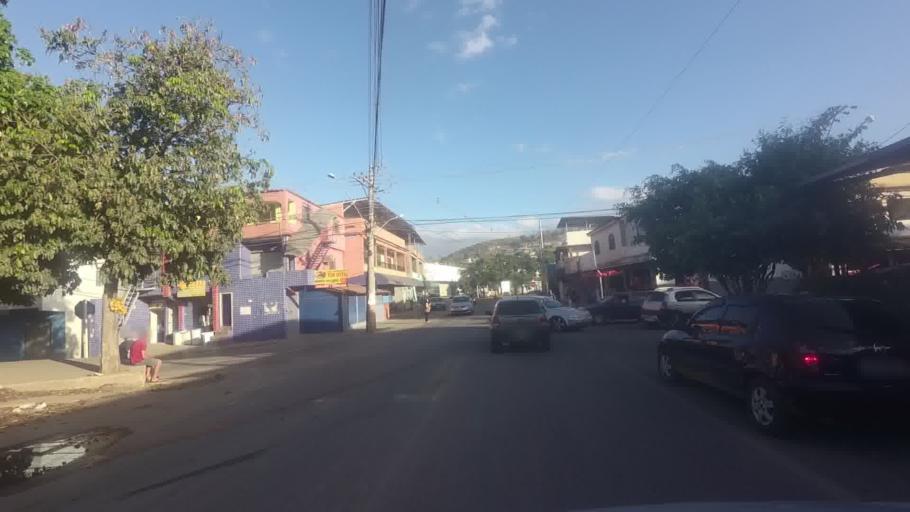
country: BR
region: Espirito Santo
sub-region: Cachoeiro De Itapemirim
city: Cachoeiro de Itapemirim
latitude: -20.8322
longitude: -41.1781
